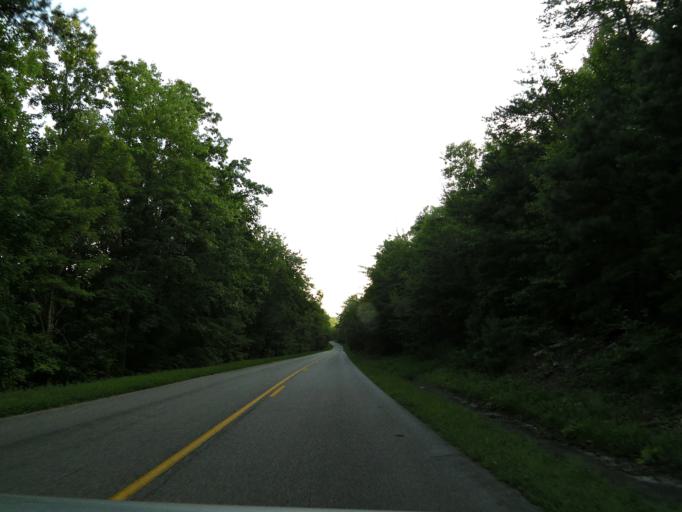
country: US
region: Tennessee
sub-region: Blount County
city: Maryville
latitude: 35.6407
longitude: -83.9348
